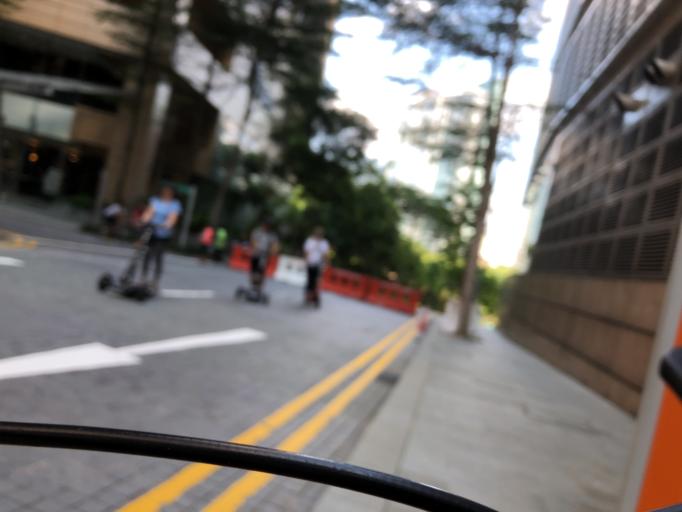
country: SG
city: Singapore
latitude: 1.3040
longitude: 103.7921
